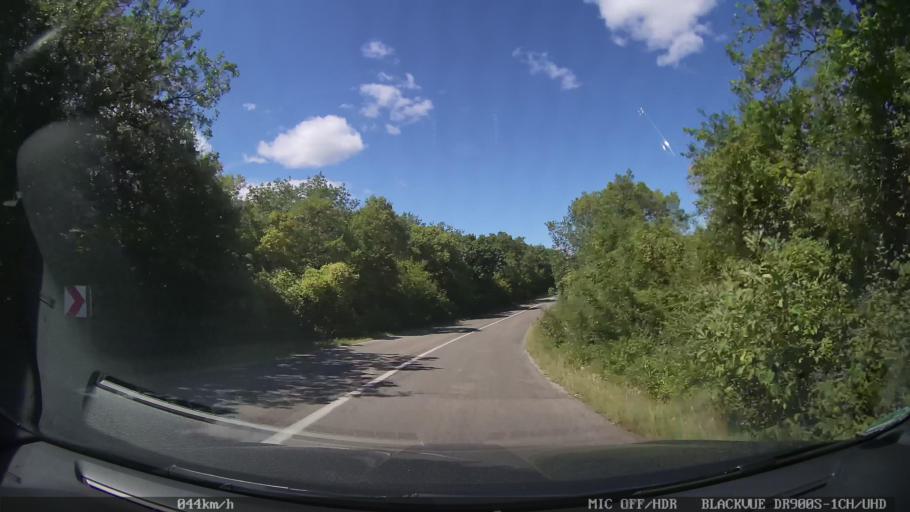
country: HR
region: Primorsko-Goranska
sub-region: Grad Krk
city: Krk
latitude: 45.0461
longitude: 14.5114
